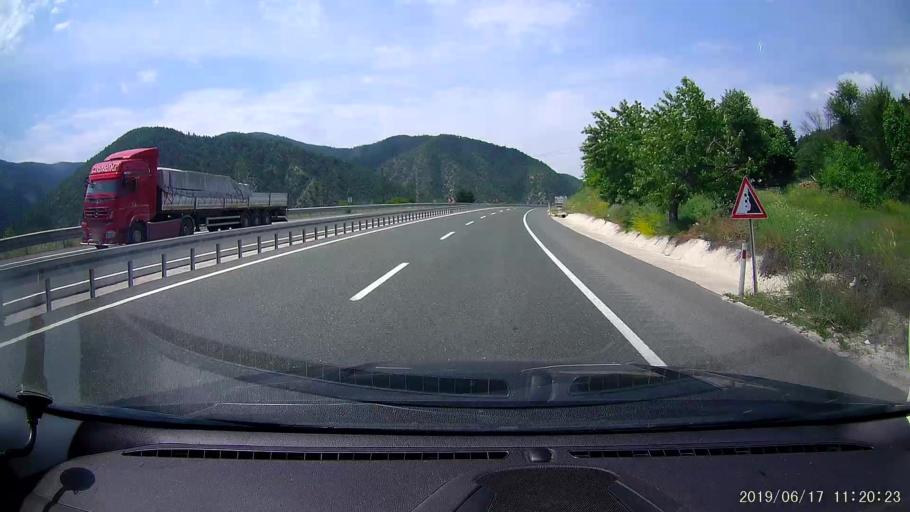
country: TR
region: Cankiri
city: Yaprakli
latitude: 40.9126
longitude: 33.8091
